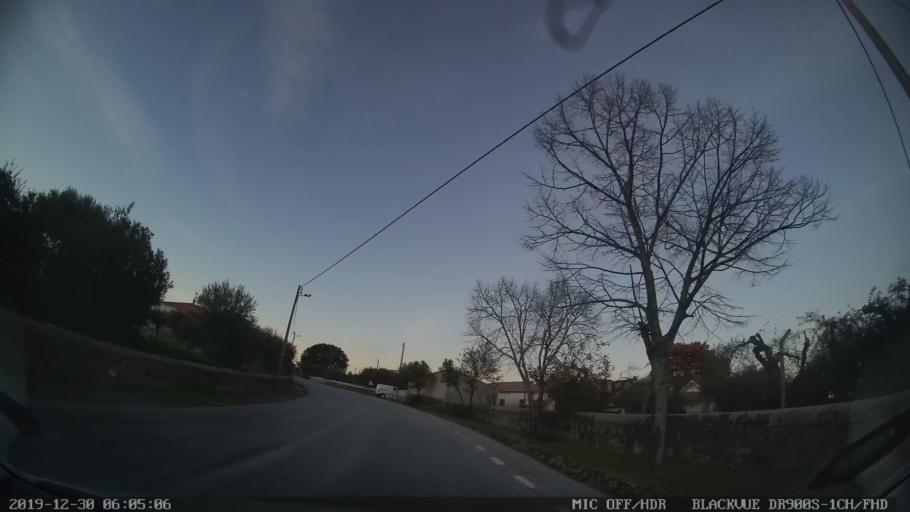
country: PT
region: Castelo Branco
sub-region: Penamacor
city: Penamacor
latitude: 40.0881
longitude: -7.2351
